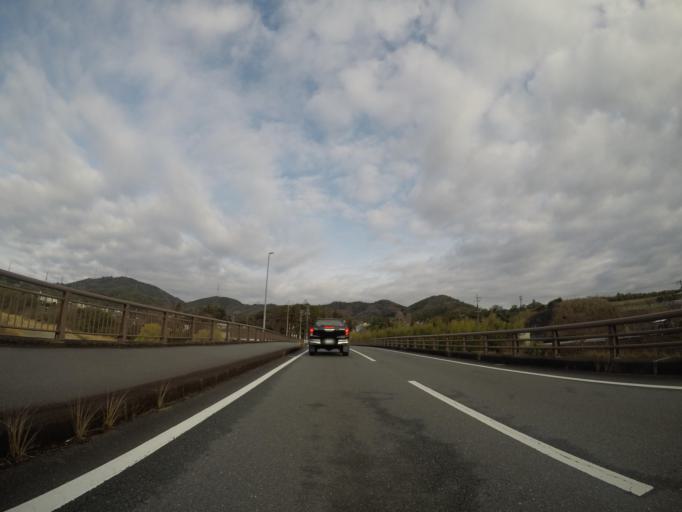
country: JP
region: Shizuoka
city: Hamakita
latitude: 34.8281
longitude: 137.7232
